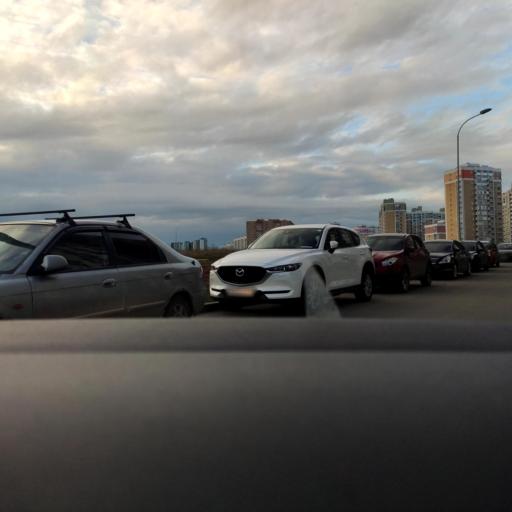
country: RU
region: Moskovskaya
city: Vidnoye
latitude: 55.5308
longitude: 37.7214
